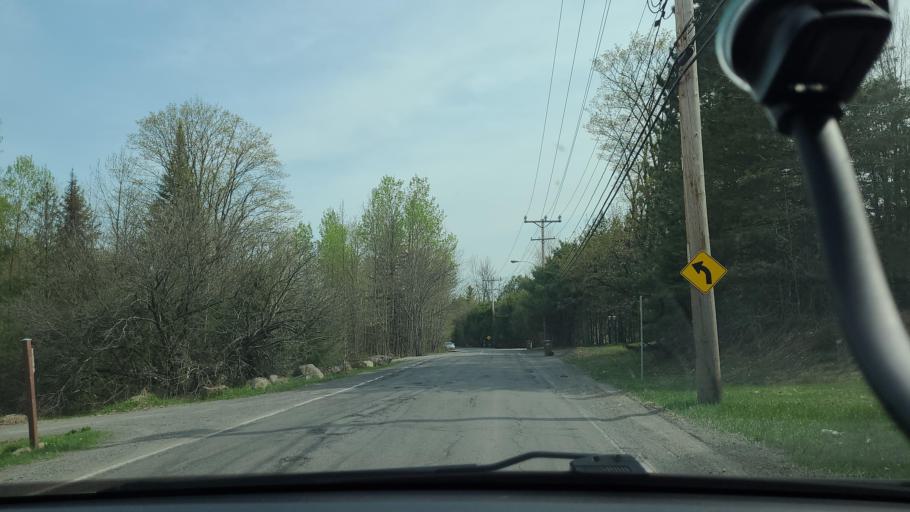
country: CA
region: Quebec
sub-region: Laurentides
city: Prevost
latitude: 45.8862
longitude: -74.0590
